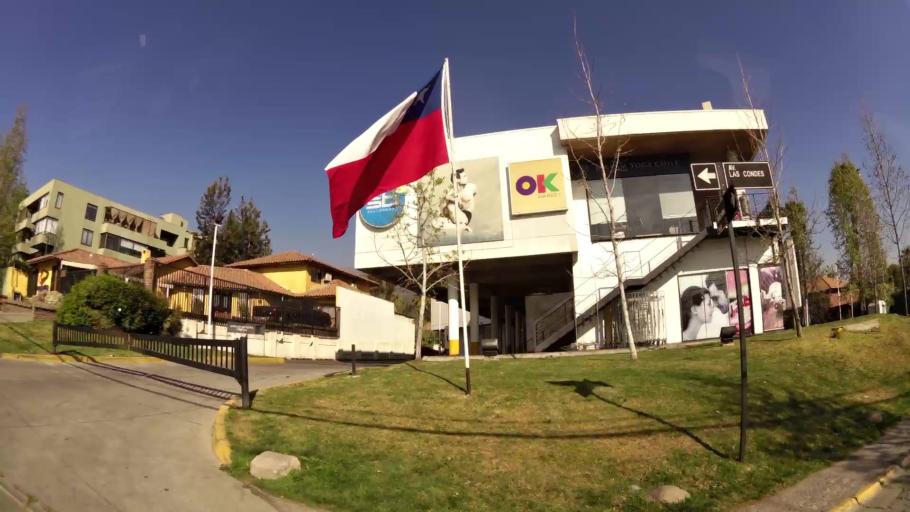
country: CL
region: Santiago Metropolitan
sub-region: Provincia de Santiago
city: Villa Presidente Frei, Nunoa, Santiago, Chile
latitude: -33.3684
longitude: -70.5012
